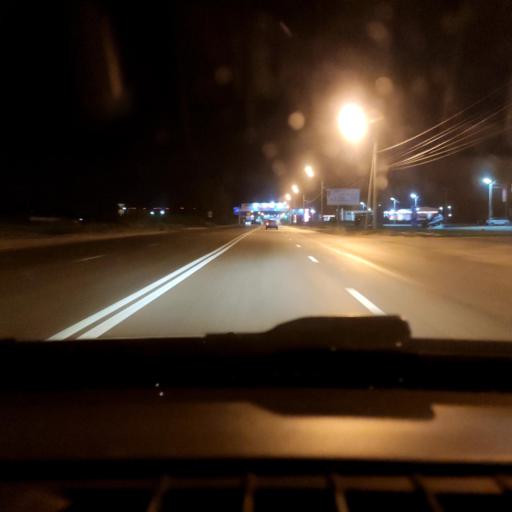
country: RU
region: Voronezj
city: Somovo
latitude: 51.6779
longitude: 39.2907
